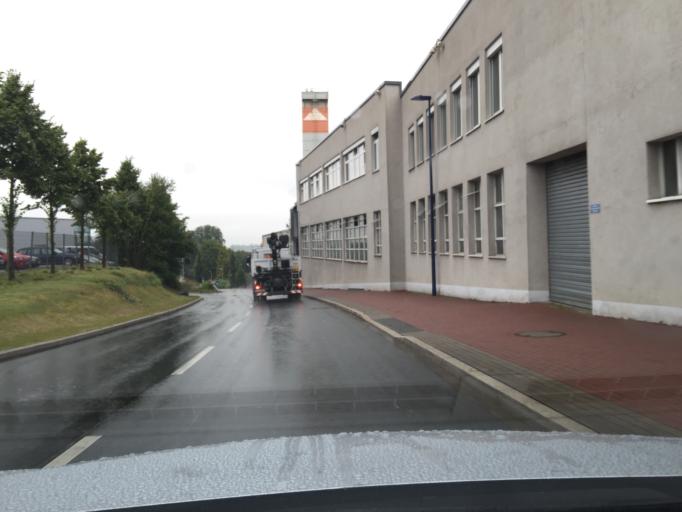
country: DE
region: North Rhine-Westphalia
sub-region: Regierungsbezirk Dusseldorf
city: Heiligenhaus
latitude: 51.3296
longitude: 6.9813
